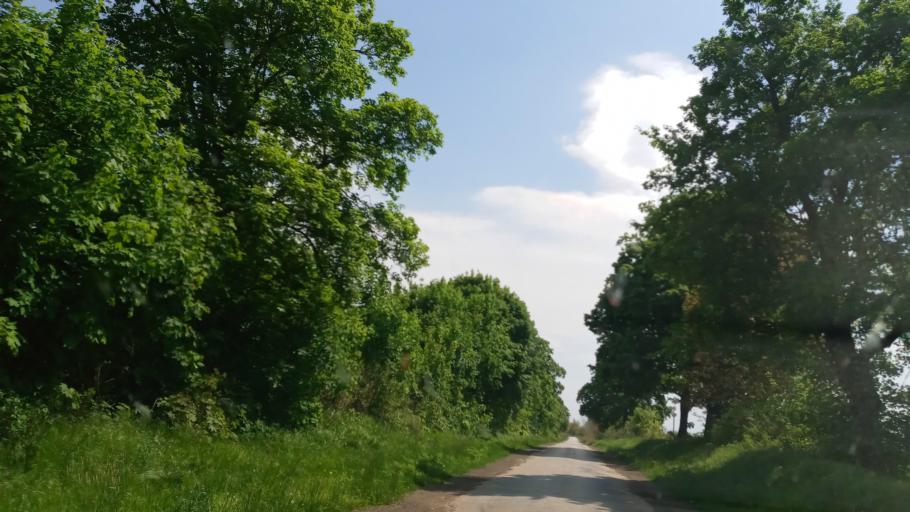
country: HU
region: Baranya
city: Villany
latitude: 45.8264
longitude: 18.5032
